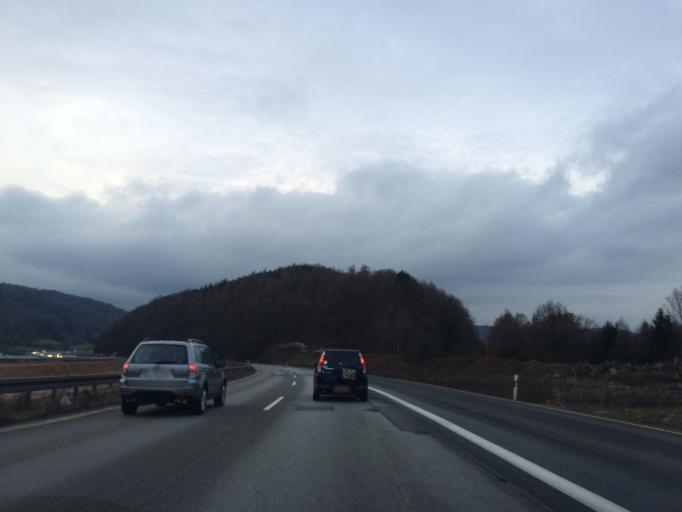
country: DE
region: Bavaria
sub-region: Regierungsbezirk Unterfranken
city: Waldaschaff
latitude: 49.9599
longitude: 9.3200
